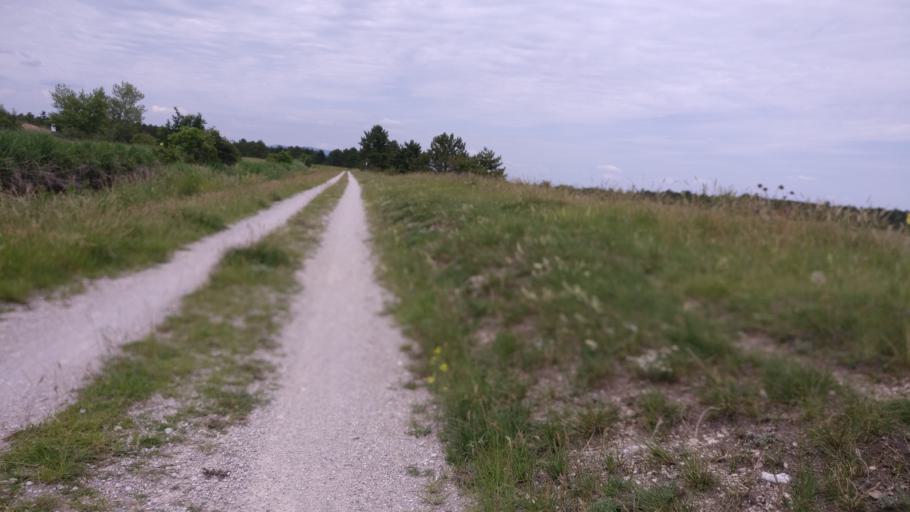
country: AT
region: Lower Austria
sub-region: Politischer Bezirk Wiener Neustadt
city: Sollenau
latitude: 47.8884
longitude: 16.2794
